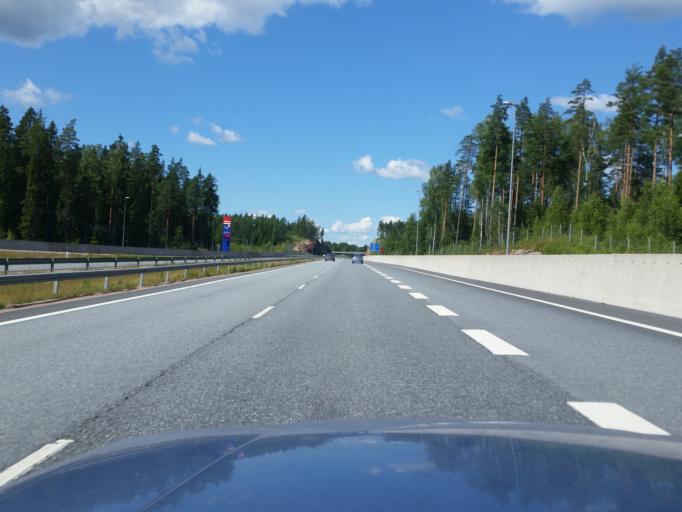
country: FI
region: Varsinais-Suomi
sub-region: Salo
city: Suomusjaervi
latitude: 60.3823
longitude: 23.6149
